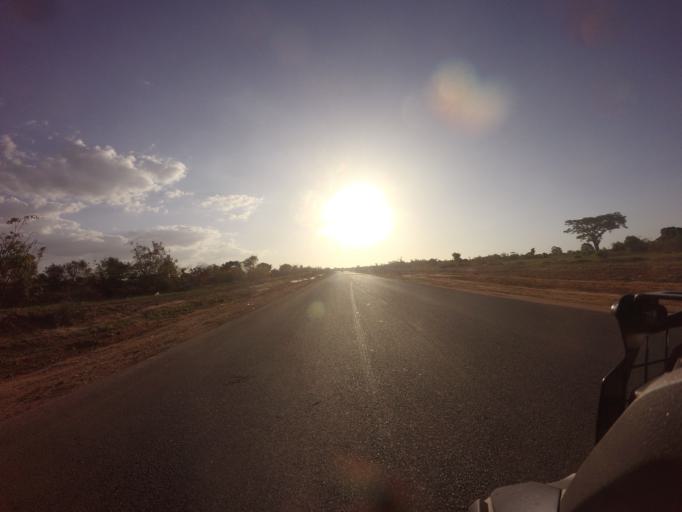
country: AO
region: Huila
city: Lubango
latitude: -14.8142
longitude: 13.6409
